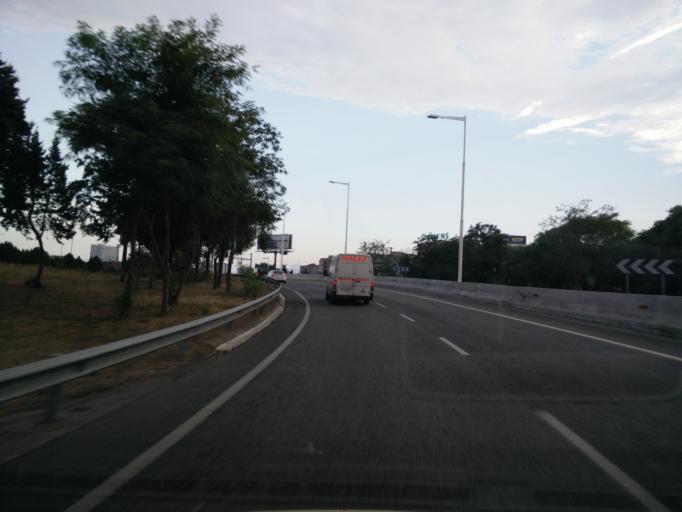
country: ES
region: Catalonia
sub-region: Provincia de Barcelona
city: Sant Adria de Besos
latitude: 41.4253
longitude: 2.2154
